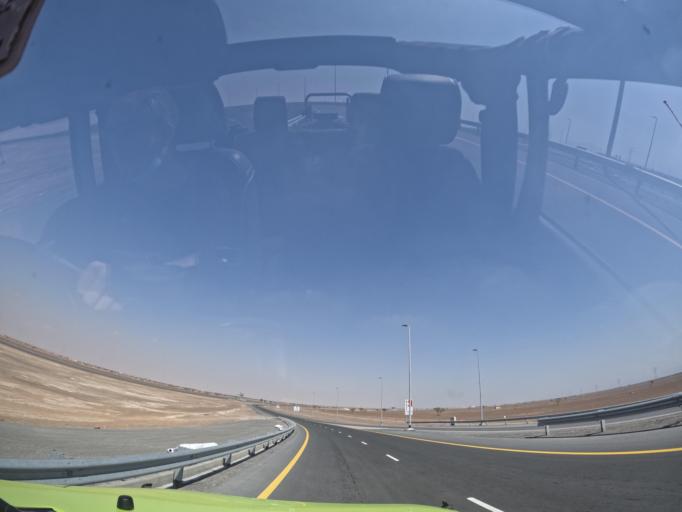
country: AE
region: Ash Shariqah
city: Adh Dhayd
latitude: 24.9110
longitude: 55.8040
